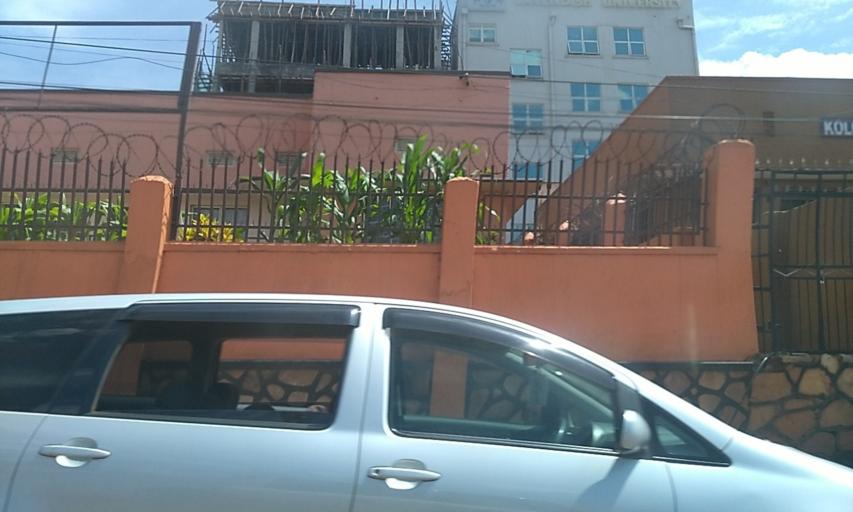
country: UG
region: Central Region
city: Kampala Central Division
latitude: 0.3411
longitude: 32.5885
